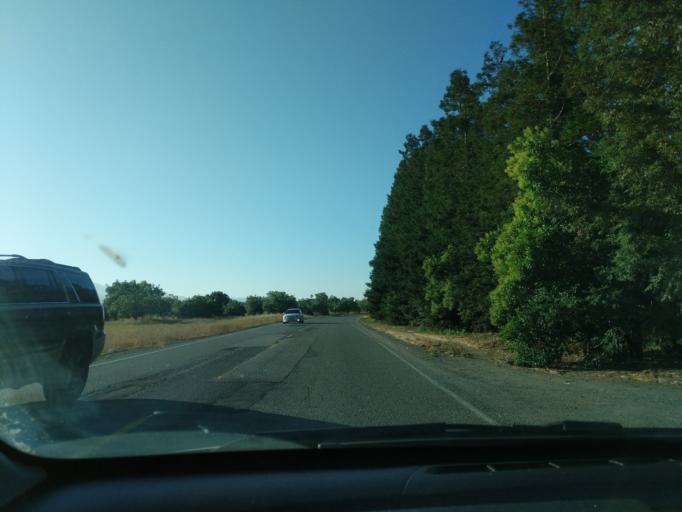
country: US
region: California
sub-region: Santa Clara County
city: Morgan Hill
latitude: 37.1377
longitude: -121.6337
